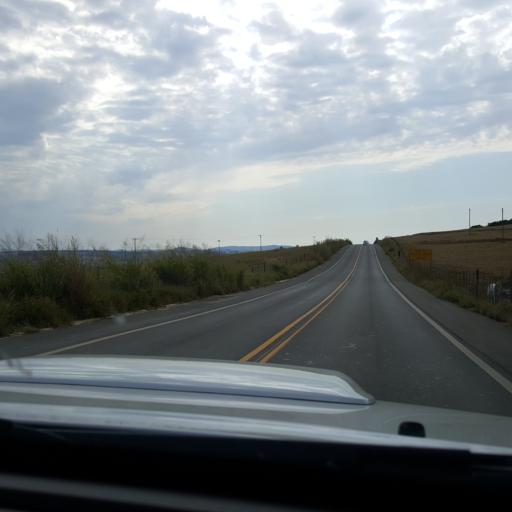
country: BR
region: Sao Paulo
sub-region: Itaporanga
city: Itaporanga
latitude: -23.7657
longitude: -49.4470
